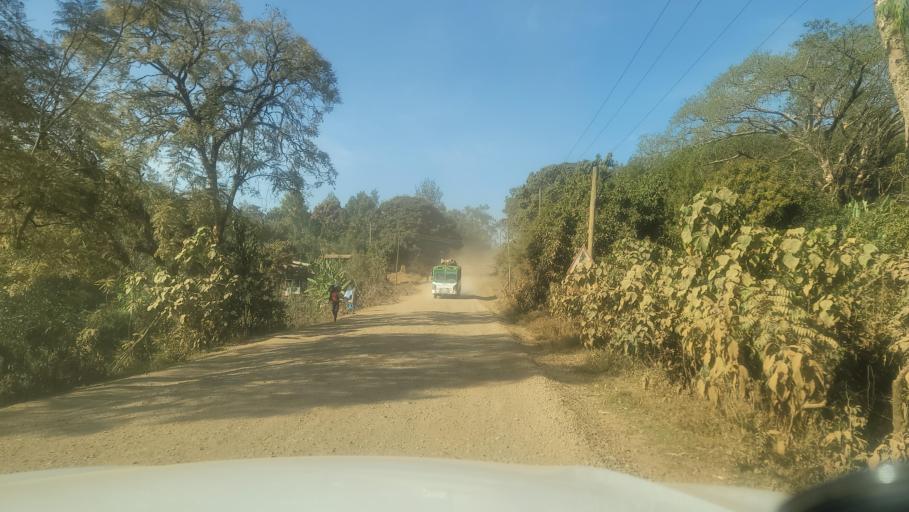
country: ET
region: Oromiya
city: Agaro
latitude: 7.8390
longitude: 36.5568
